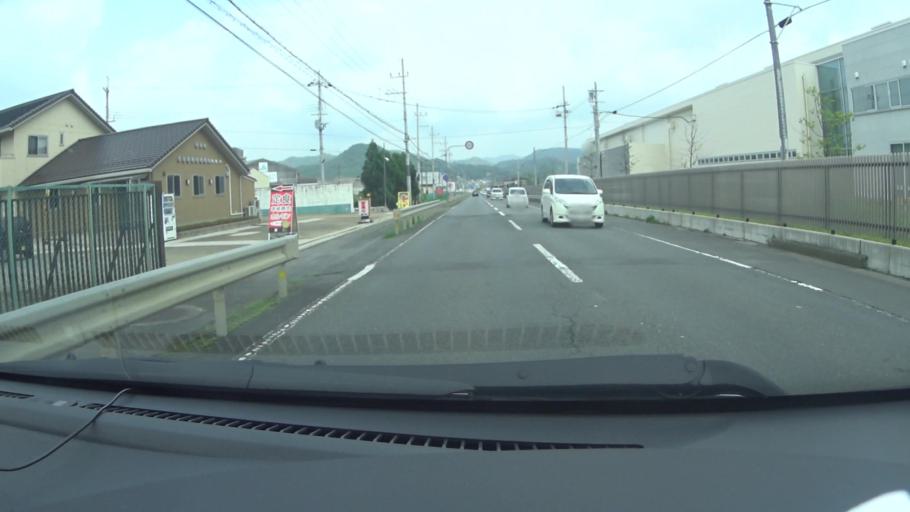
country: JP
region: Kyoto
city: Ayabe
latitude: 35.1784
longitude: 135.4216
